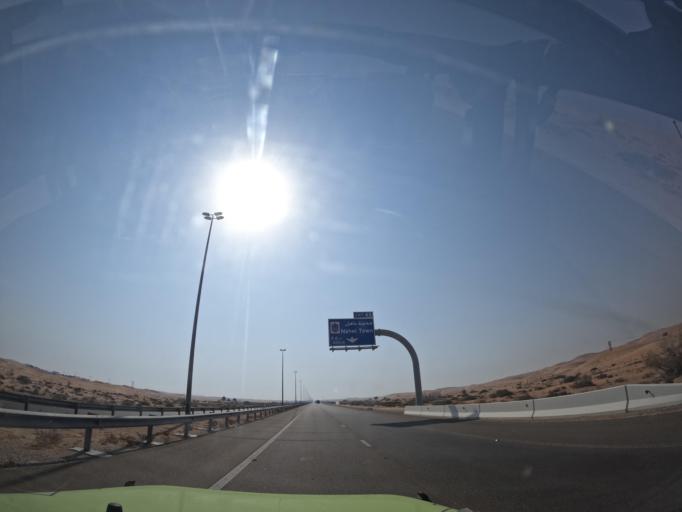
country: OM
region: Al Buraimi
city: Al Buraymi
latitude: 24.5163
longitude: 55.5590
